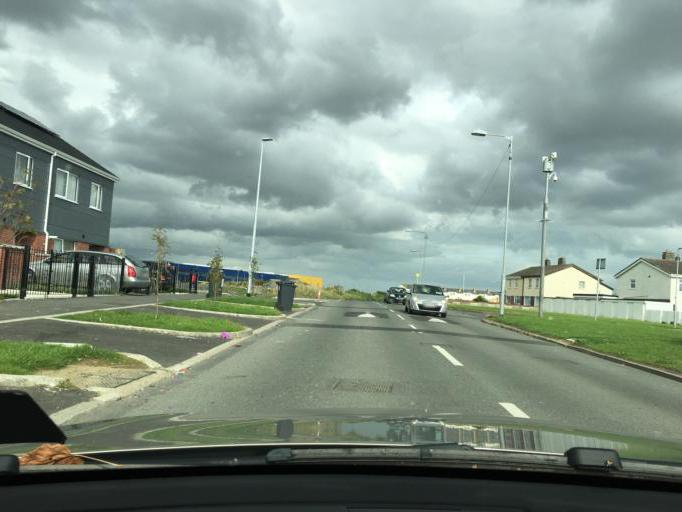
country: IE
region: Leinster
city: Ballymun
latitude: 53.4045
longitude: -6.2804
